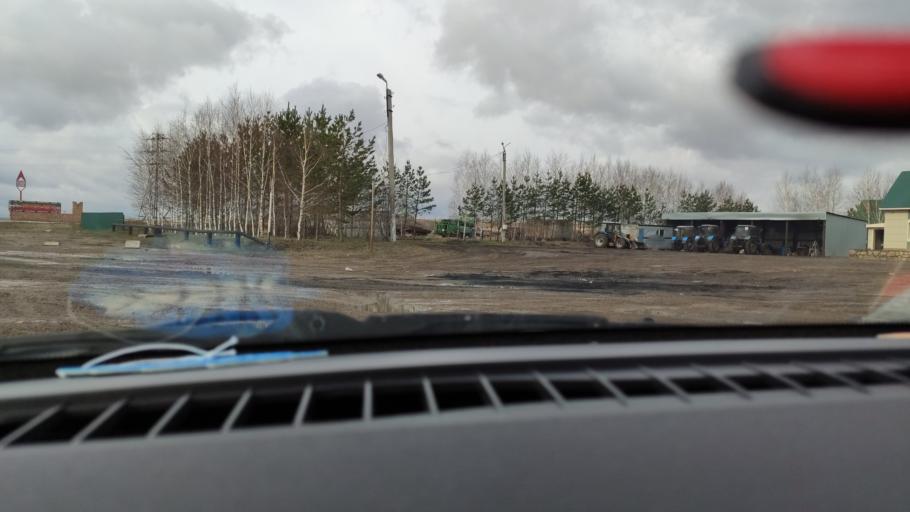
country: RU
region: Tatarstan
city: Cheremshan
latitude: 54.8604
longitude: 51.5932
